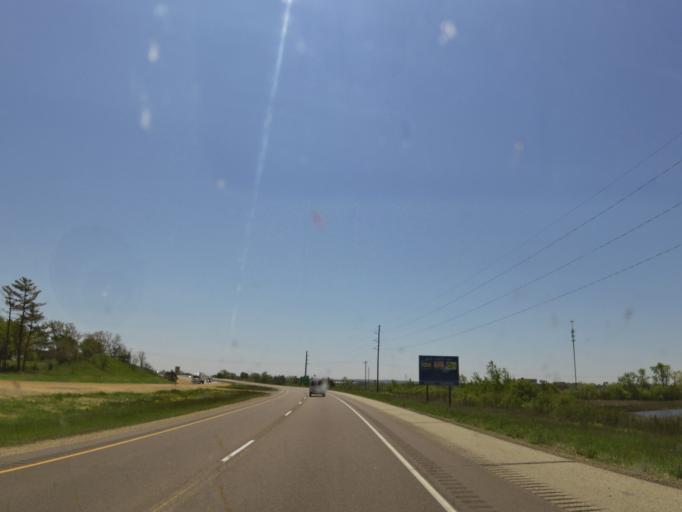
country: US
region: Wisconsin
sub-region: Monroe County
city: Tomah
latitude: 44.0269
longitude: -90.5120
